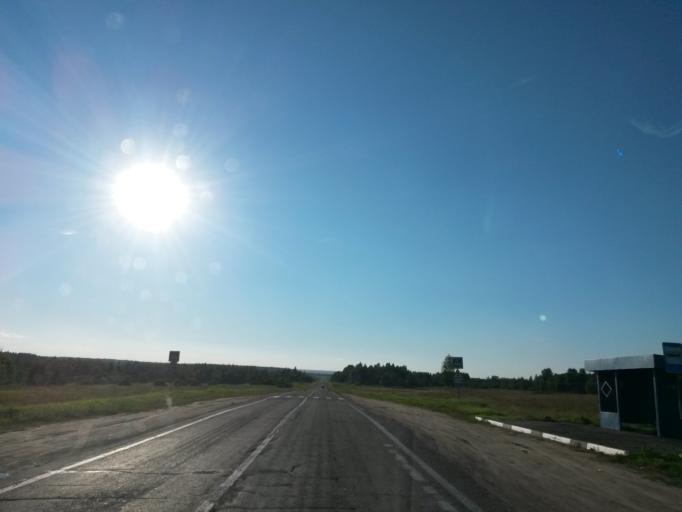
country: RU
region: Jaroslavl
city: Gavrilov-Yam
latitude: 57.2762
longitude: 39.9304
